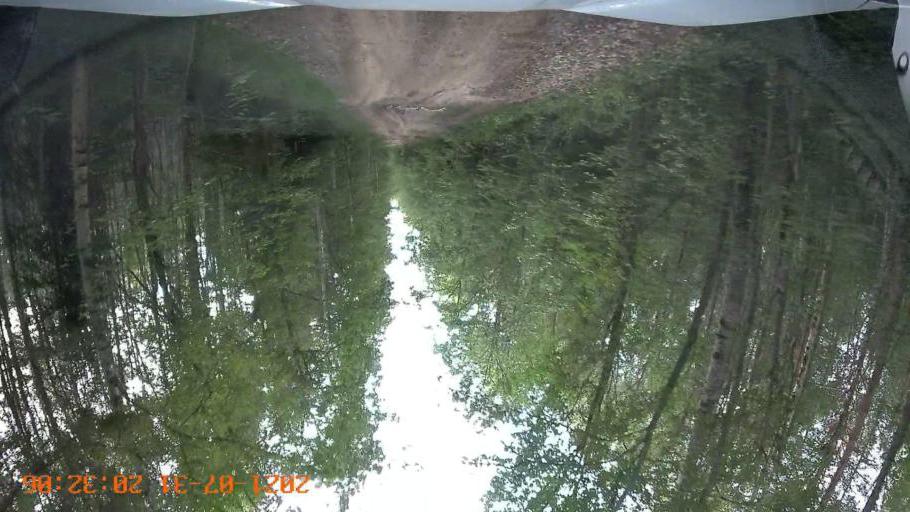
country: RU
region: Republic of Karelia
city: Pudozh
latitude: 61.6613
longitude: 36.2755
